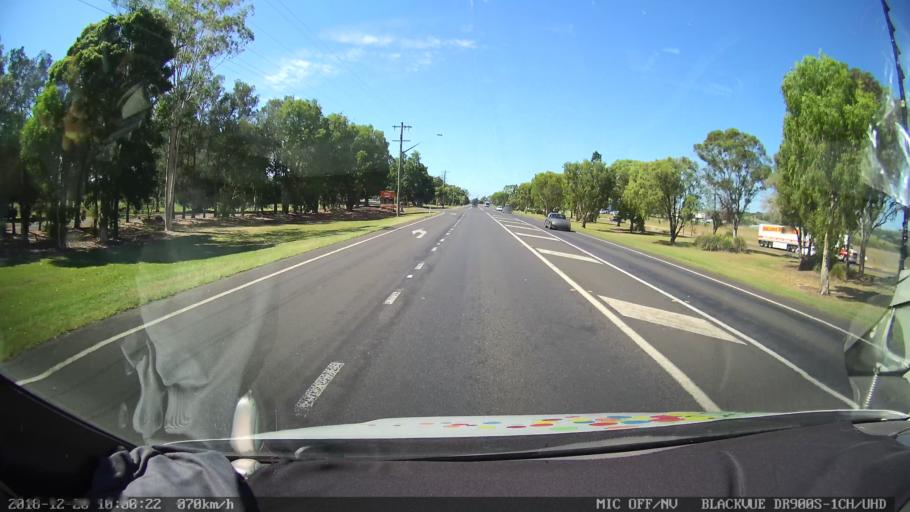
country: AU
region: New South Wales
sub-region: Lismore Municipality
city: Lismore
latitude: -28.8317
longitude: 153.2648
